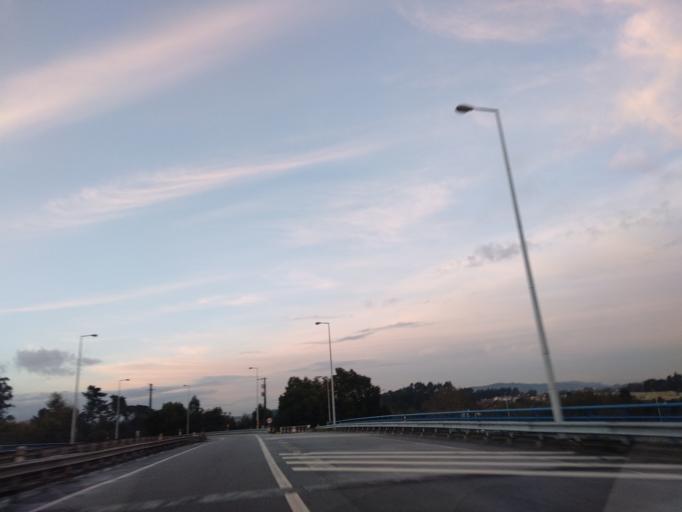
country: PT
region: Braga
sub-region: Vila Nova de Famalicao
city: Vila Nova de Famalicao
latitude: 41.3819
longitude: -8.5029
